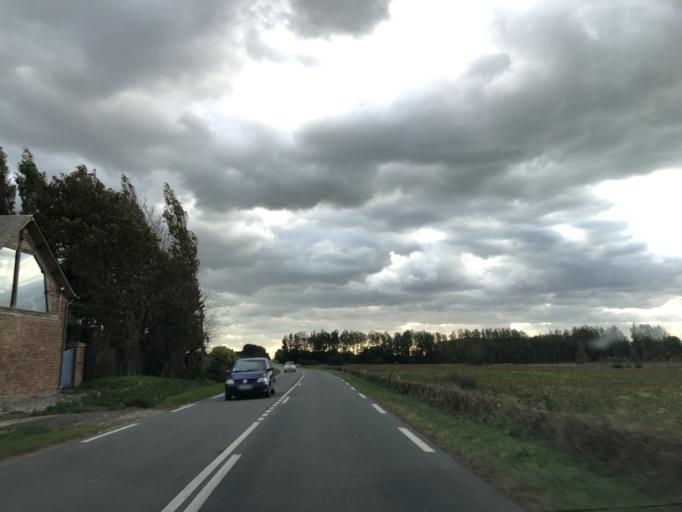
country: FR
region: Picardie
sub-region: Departement de la Somme
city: Cayeux-sur-Mer
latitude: 50.1307
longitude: 1.5021
